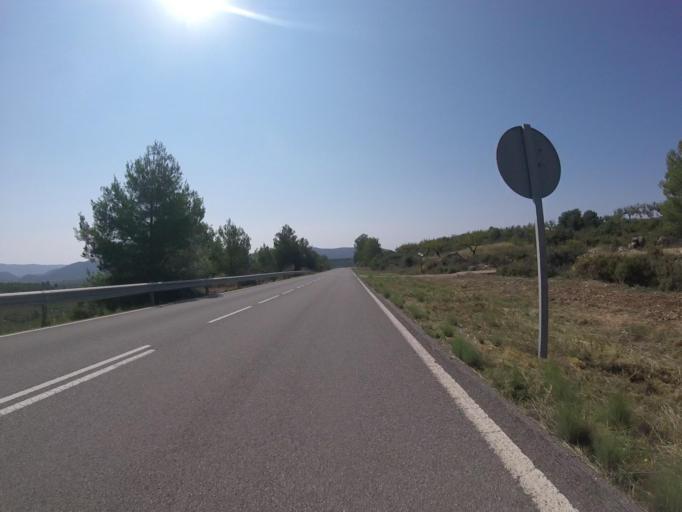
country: ES
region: Valencia
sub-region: Provincia de Castello
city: Adzaneta
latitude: 40.2409
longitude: -0.1888
